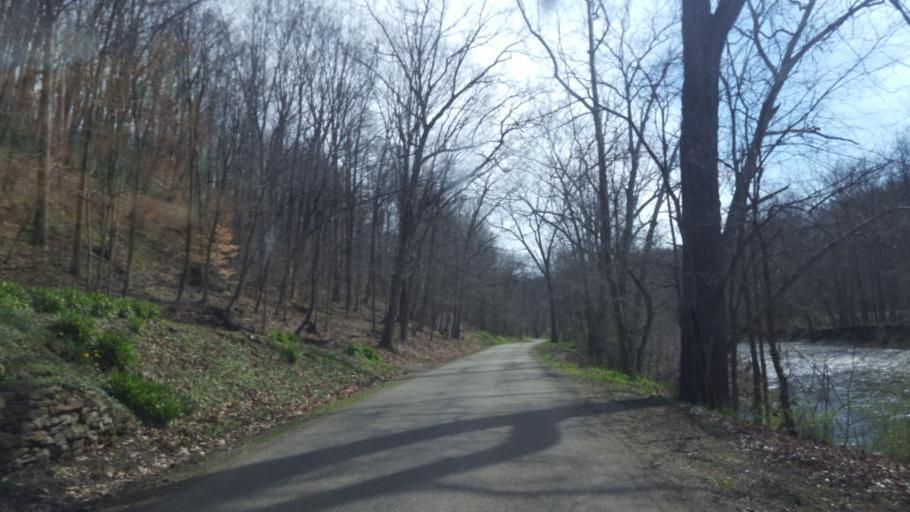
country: US
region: Ohio
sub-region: Knox County
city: Gambier
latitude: 40.3773
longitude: -82.4405
